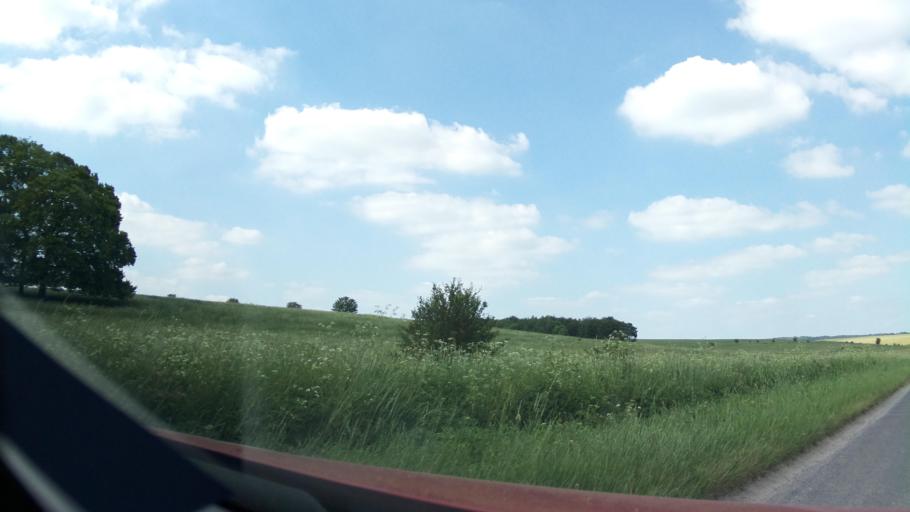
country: GB
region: England
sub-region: Wiltshire
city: Milston
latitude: 51.2611
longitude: -1.7278
